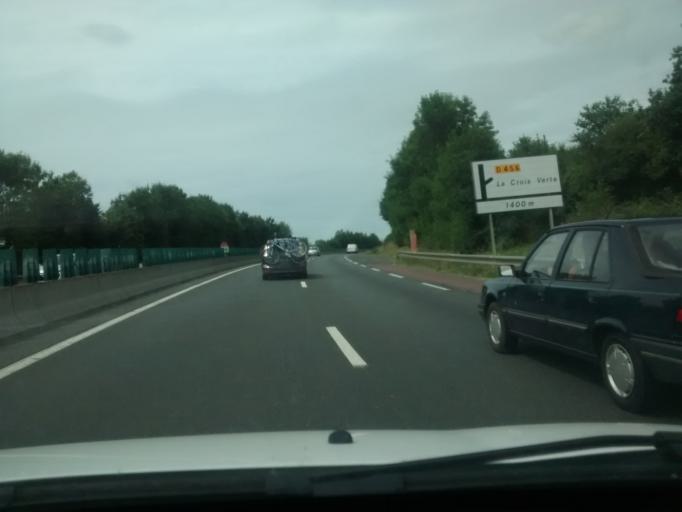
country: FR
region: Lower Normandy
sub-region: Departement de la Manche
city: Le Val-Saint-Pere
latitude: 48.6580
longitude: -1.3611
